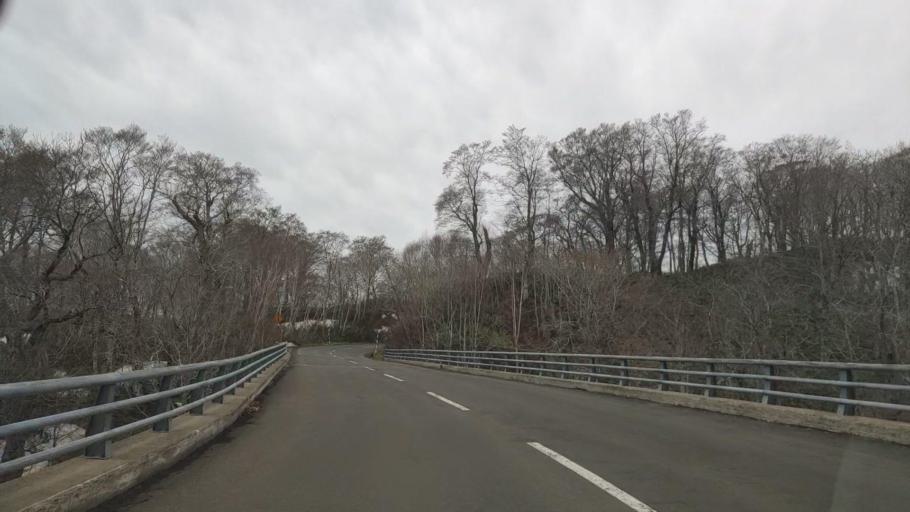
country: JP
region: Akita
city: Hanawa
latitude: 40.4180
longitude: 140.8398
